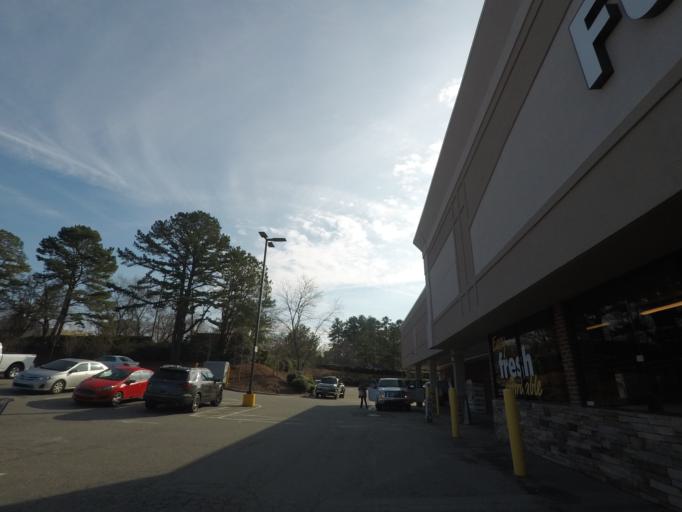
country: US
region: North Carolina
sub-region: Durham County
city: Durham
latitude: 36.0763
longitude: -78.9111
